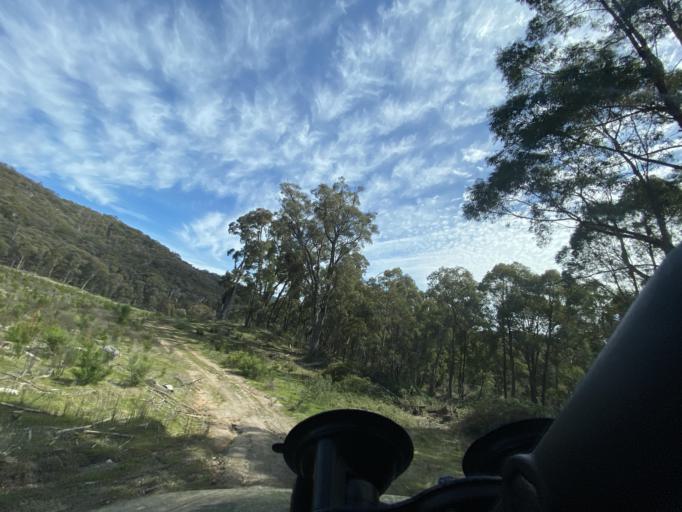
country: AU
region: Victoria
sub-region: Mansfield
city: Mansfield
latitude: -36.8309
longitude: 146.1001
